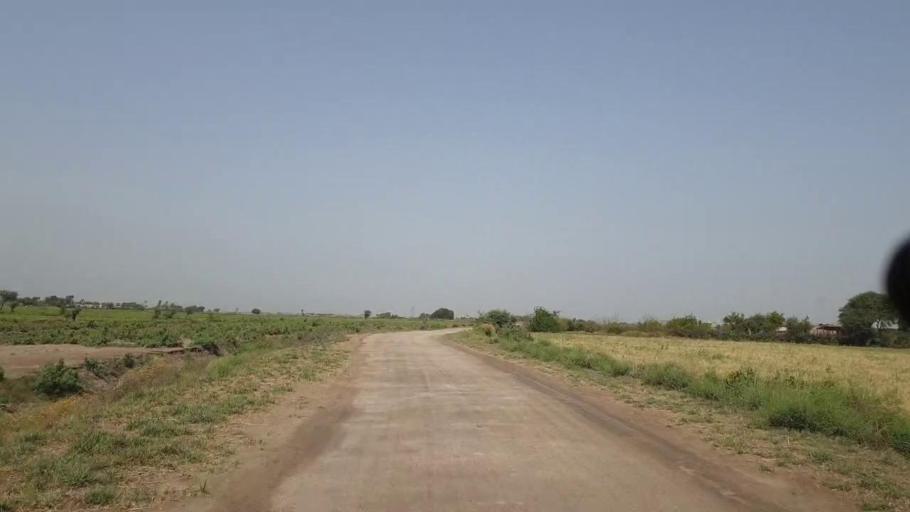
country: PK
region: Sindh
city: Matli
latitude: 25.0694
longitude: 68.6901
